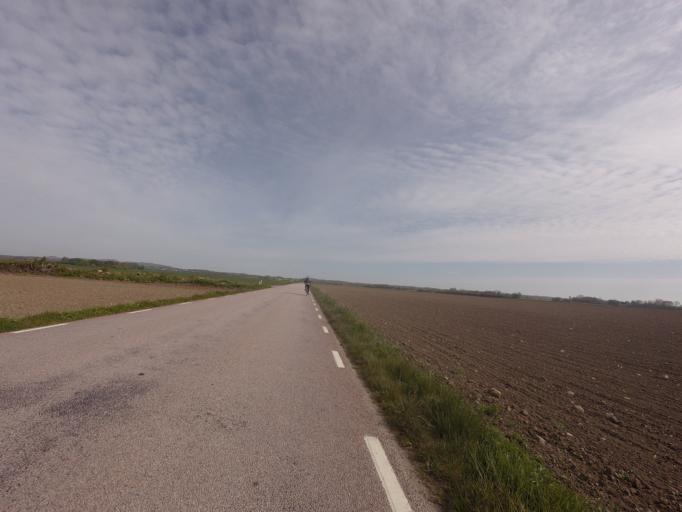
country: SE
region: Skane
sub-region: Hoganas Kommun
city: Hoganas
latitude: 56.2328
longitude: 12.5862
